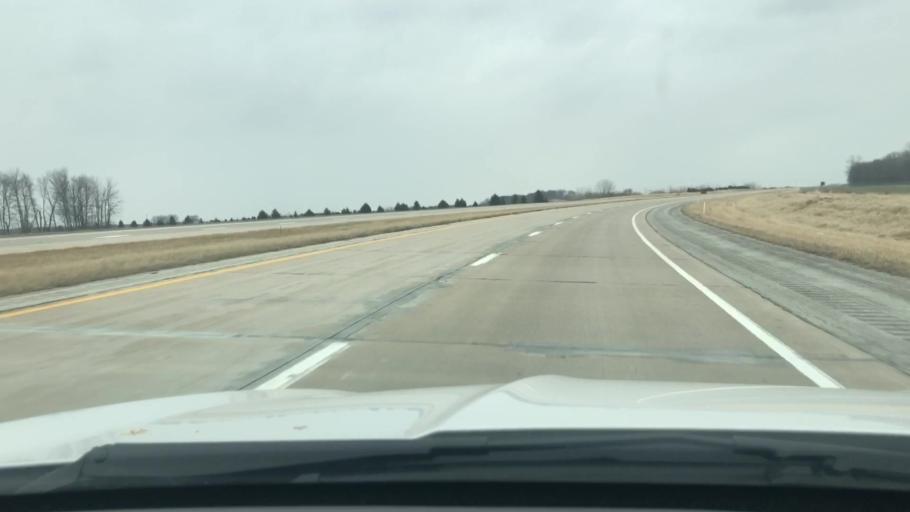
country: US
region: Indiana
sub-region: Cass County
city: Logansport
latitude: 40.7364
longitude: -86.2982
